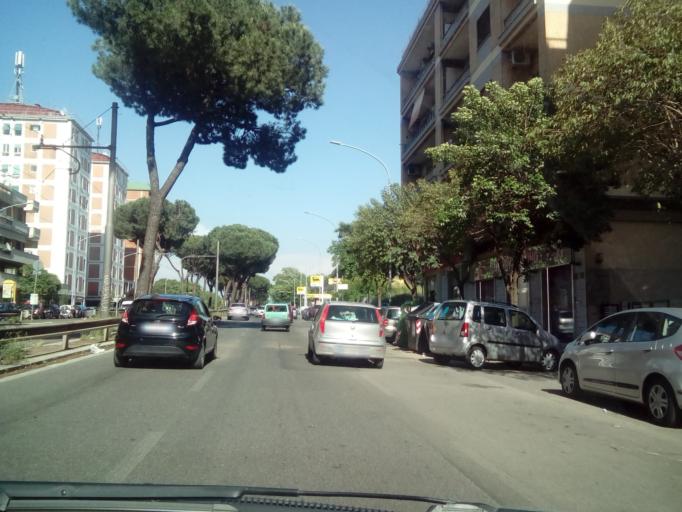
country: IT
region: Latium
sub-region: Citta metropolitana di Roma Capitale
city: Rome
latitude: 41.8949
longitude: 12.5643
